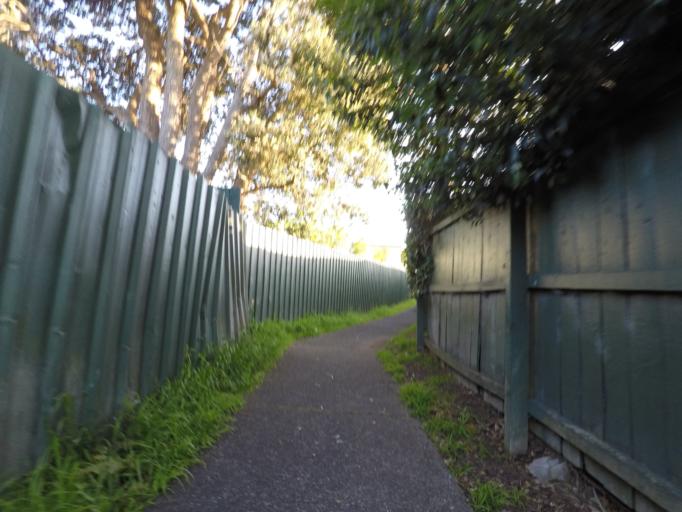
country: NZ
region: Auckland
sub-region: Auckland
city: Rosebank
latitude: -36.8447
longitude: 174.6499
